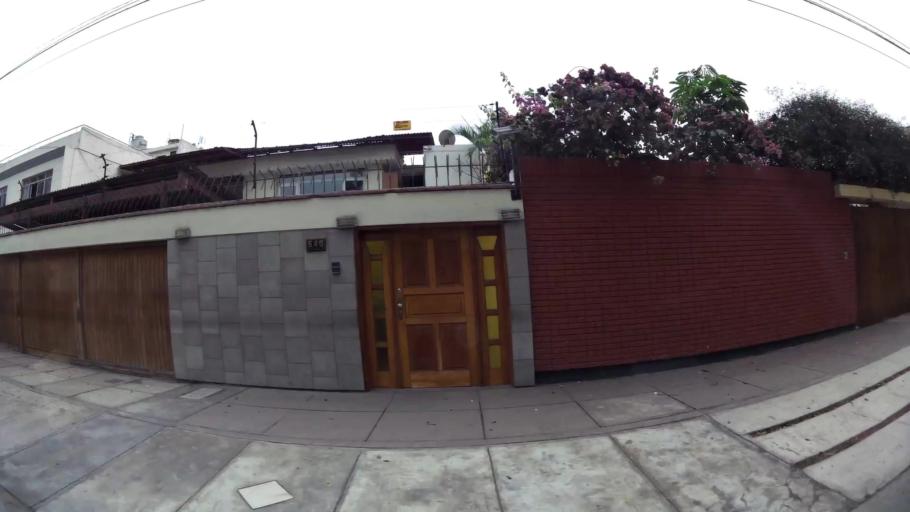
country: PE
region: Lima
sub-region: Lima
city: Surco
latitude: -12.1256
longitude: -77.0130
